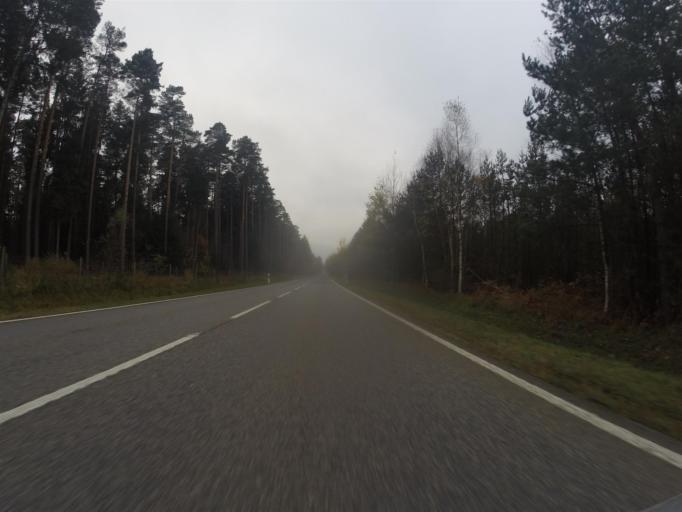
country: DE
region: Thuringia
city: Hermsdorf
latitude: 50.9100
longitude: 11.8362
